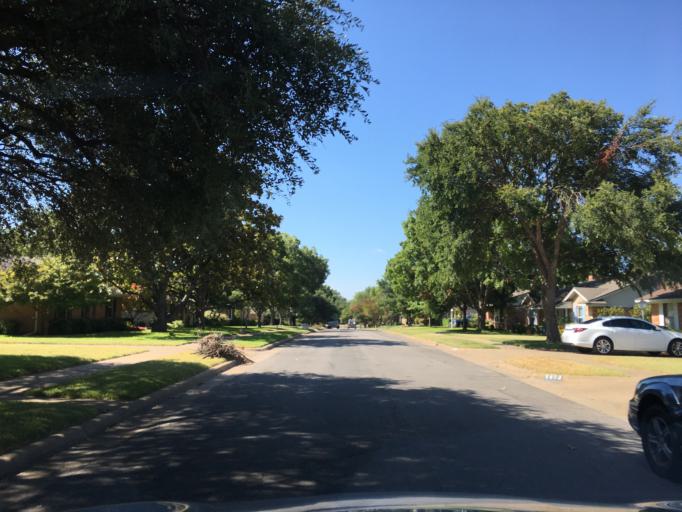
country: US
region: Texas
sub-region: Dallas County
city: Garland
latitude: 32.8665
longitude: -96.6940
